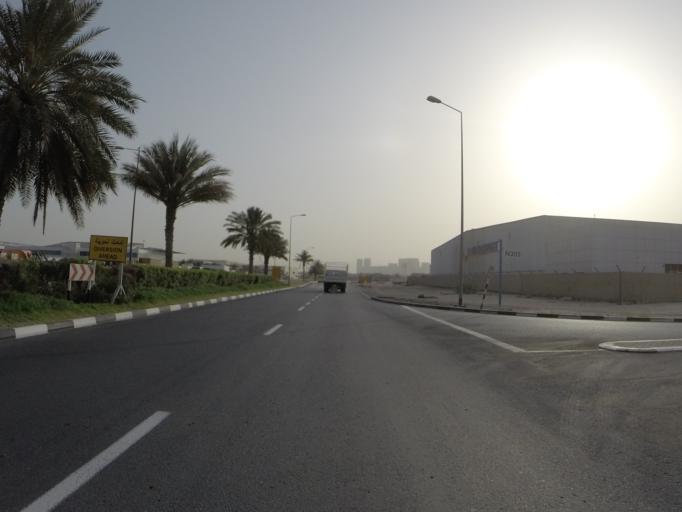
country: AE
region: Dubai
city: Dubai
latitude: 24.9686
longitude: 55.0746
